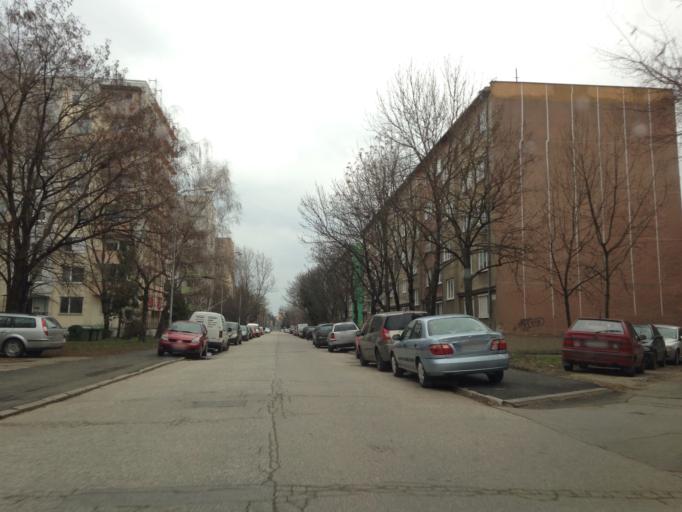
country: SK
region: Nitriansky
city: Komarno
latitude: 47.7638
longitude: 18.1204
